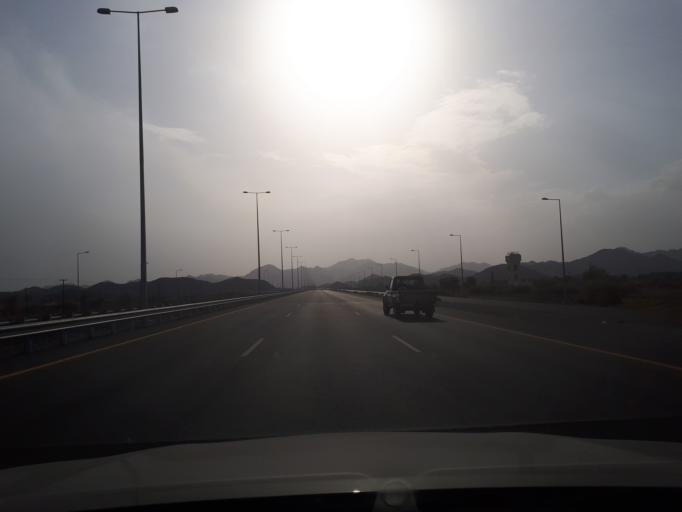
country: OM
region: Ash Sharqiyah
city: Ibra'
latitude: 22.8406
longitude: 58.3774
